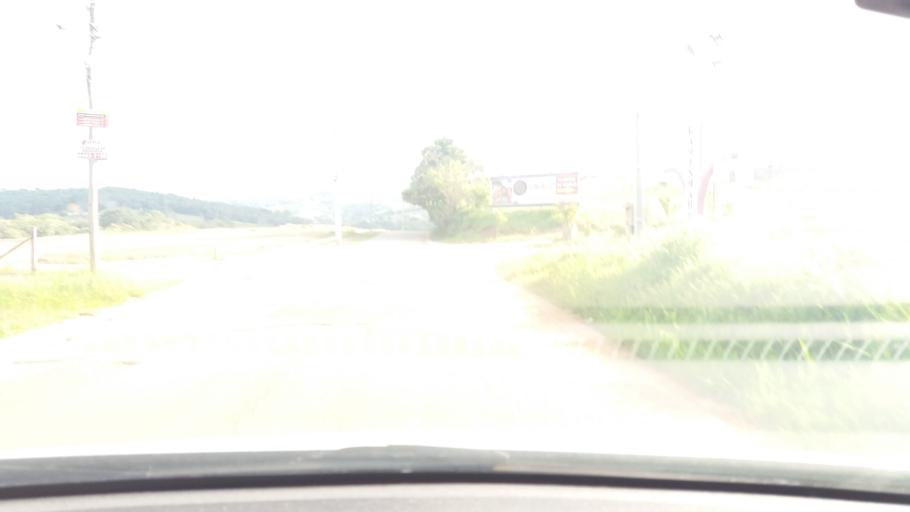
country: BR
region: Sao Paulo
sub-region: Bom Jesus Dos Perdoes
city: Bom Jesus dos Perdoes
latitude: -23.1526
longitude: -46.4717
